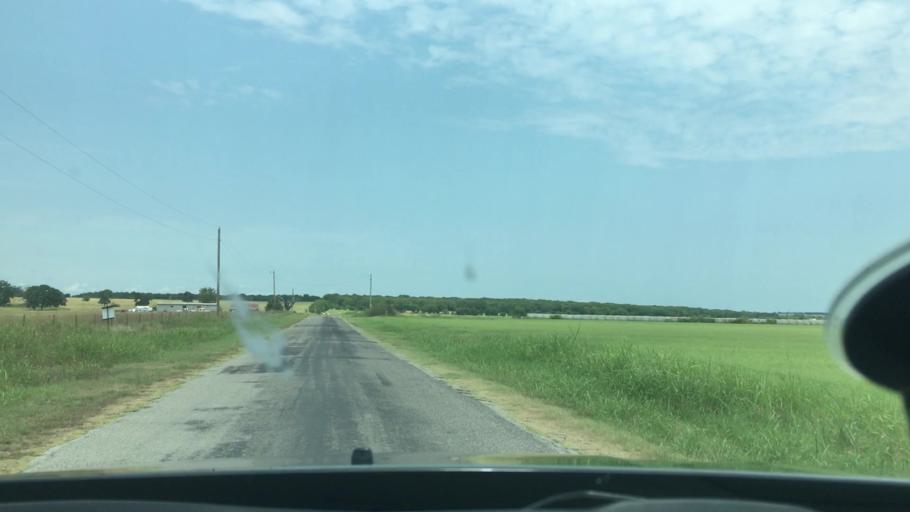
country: US
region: Texas
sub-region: Cooke County
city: Muenster
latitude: 33.8624
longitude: -97.3696
